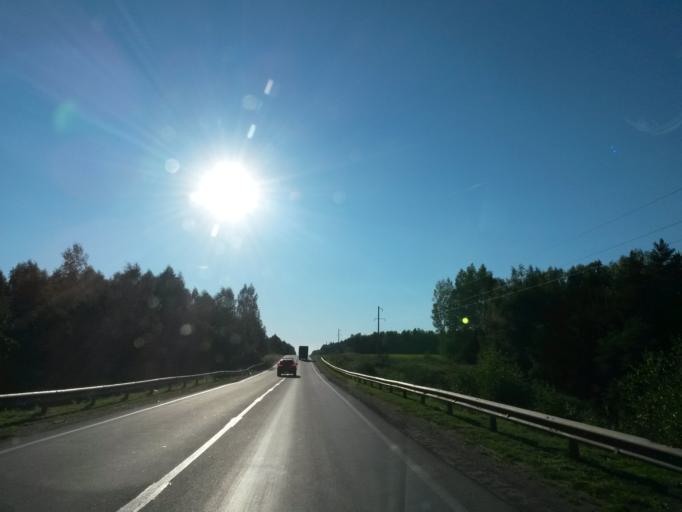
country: RU
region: Jaroslavl
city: Dubki
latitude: 57.2576
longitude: 40.0799
